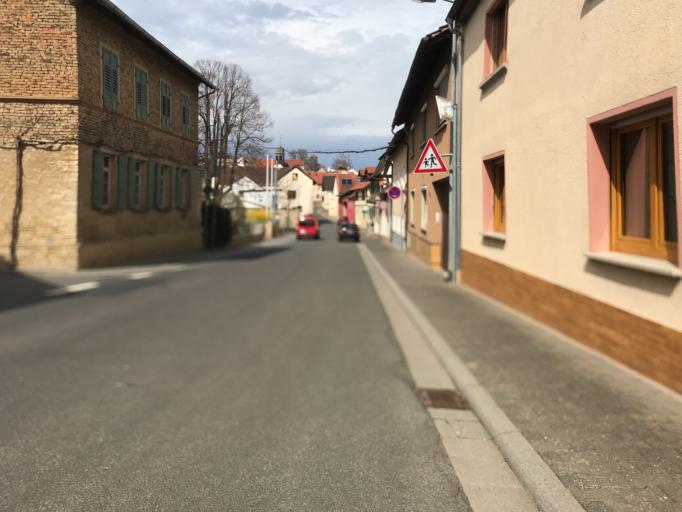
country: DE
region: Rheinland-Pfalz
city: Appenheim
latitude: 49.9287
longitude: 8.0343
